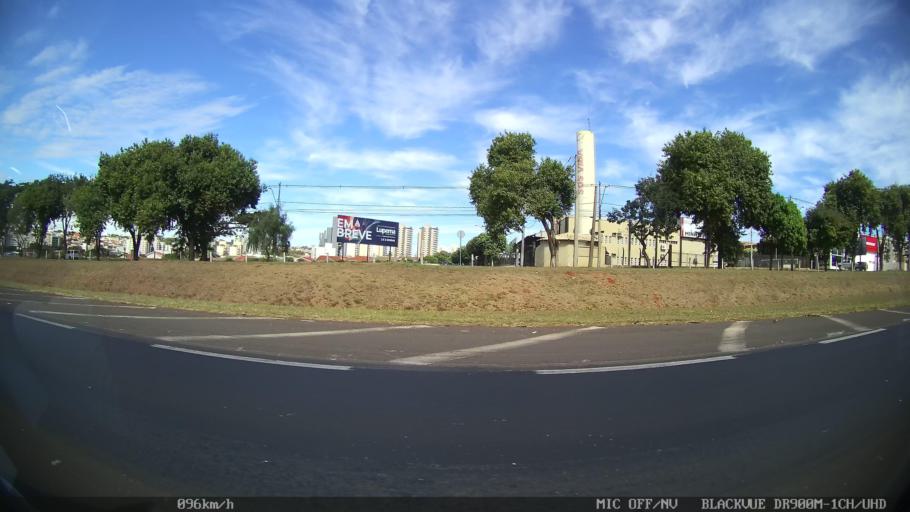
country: BR
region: Sao Paulo
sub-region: Sao Jose Do Rio Preto
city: Sao Jose do Rio Preto
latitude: -20.8249
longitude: -49.4091
